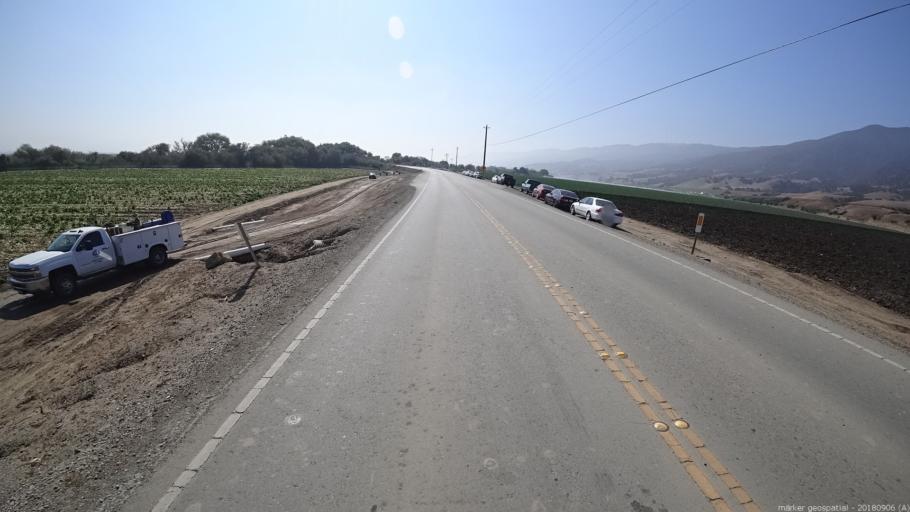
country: US
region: California
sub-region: Monterey County
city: Chualar
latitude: 36.5582
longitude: -121.5520
